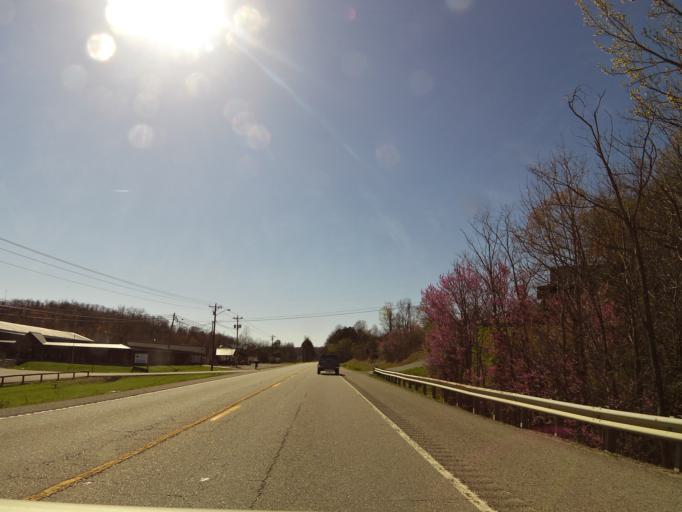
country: US
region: Tennessee
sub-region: Scott County
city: Oneida
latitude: 36.5379
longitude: -84.4690
